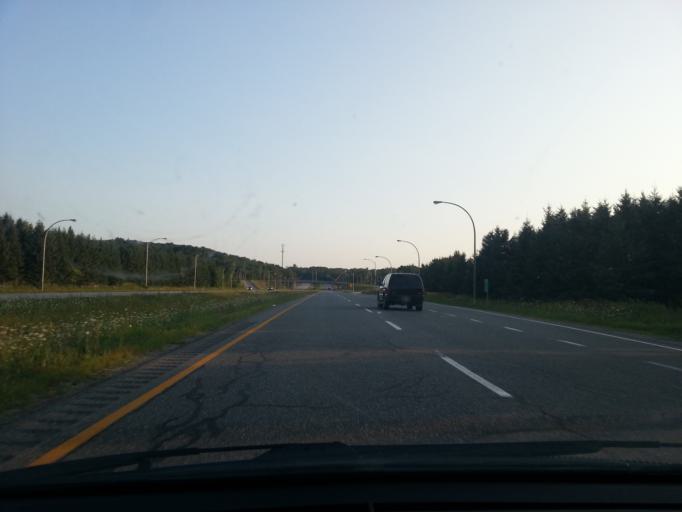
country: CA
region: Quebec
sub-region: Outaouais
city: Gatineau
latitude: 45.4986
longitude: -75.7996
